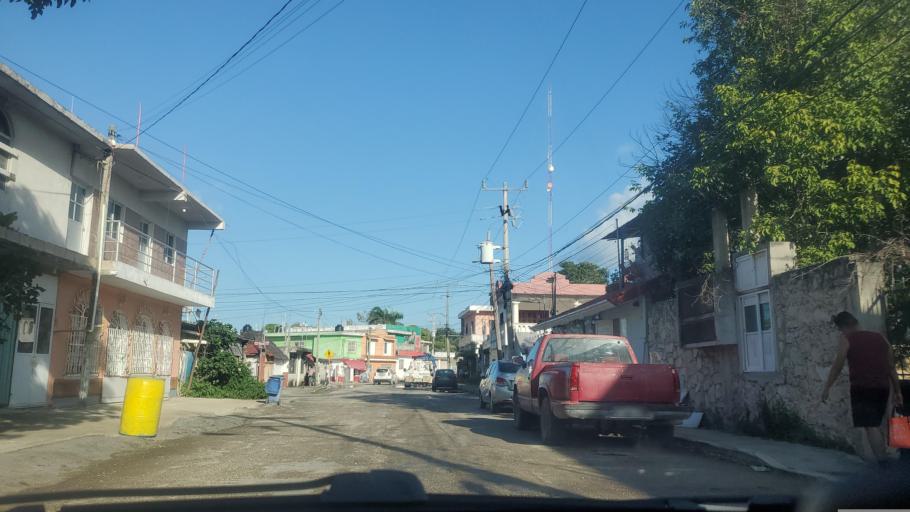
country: MX
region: Quintana Roo
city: Tulum
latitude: 20.2098
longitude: -87.4684
